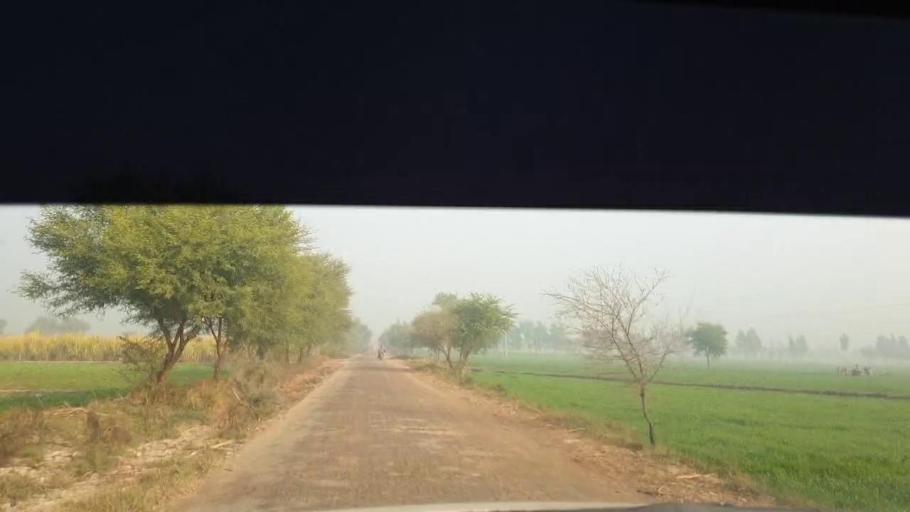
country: PK
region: Sindh
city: Berani
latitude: 25.7860
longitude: 68.7716
